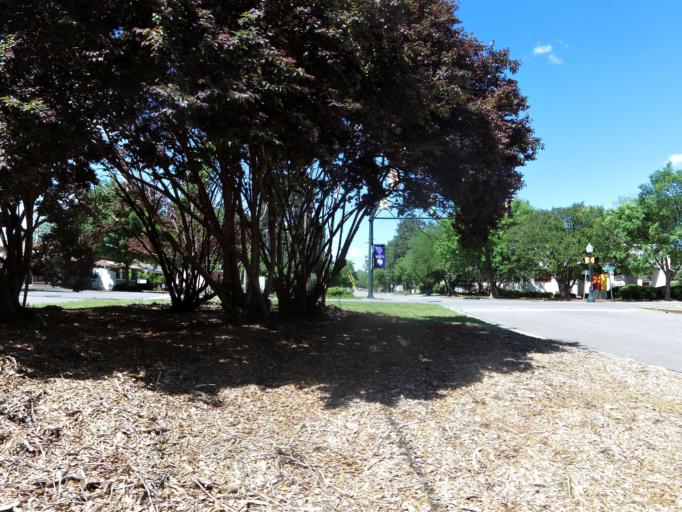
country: US
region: South Carolina
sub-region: Aiken County
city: Aiken
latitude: 33.5620
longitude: -81.7239
